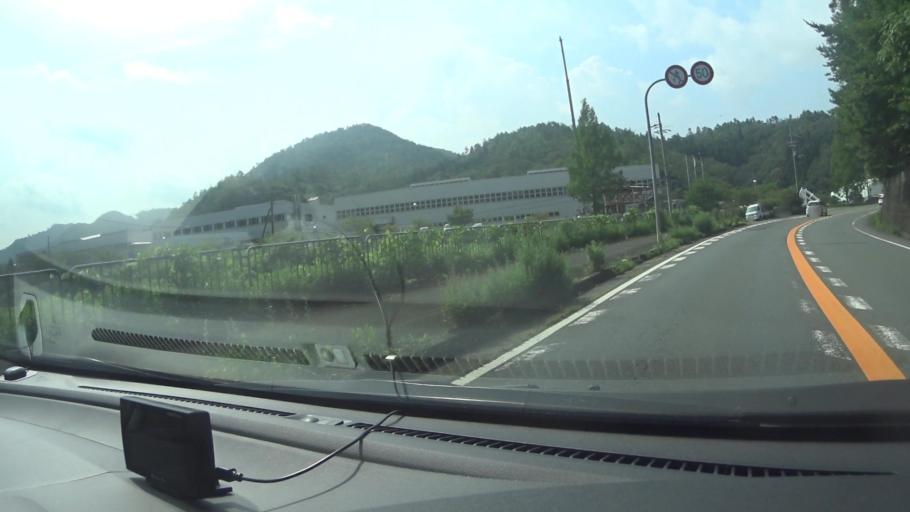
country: JP
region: Kyoto
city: Ayabe
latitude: 35.1655
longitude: 135.3607
